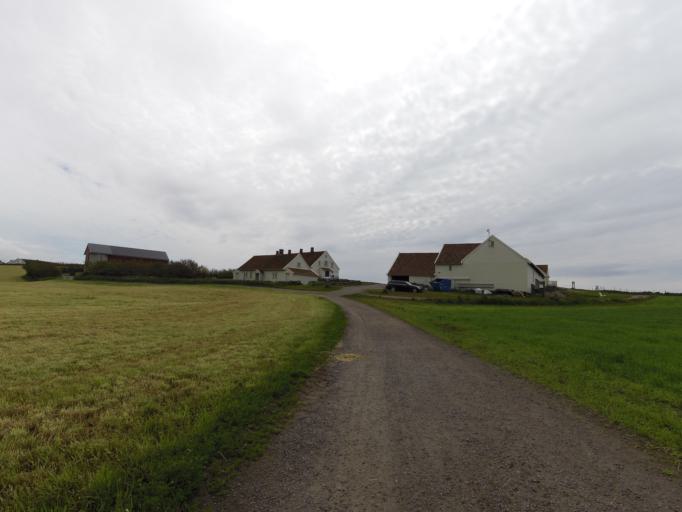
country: NO
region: Rogaland
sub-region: Ha
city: Naerbo
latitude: 58.6677
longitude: 5.5518
